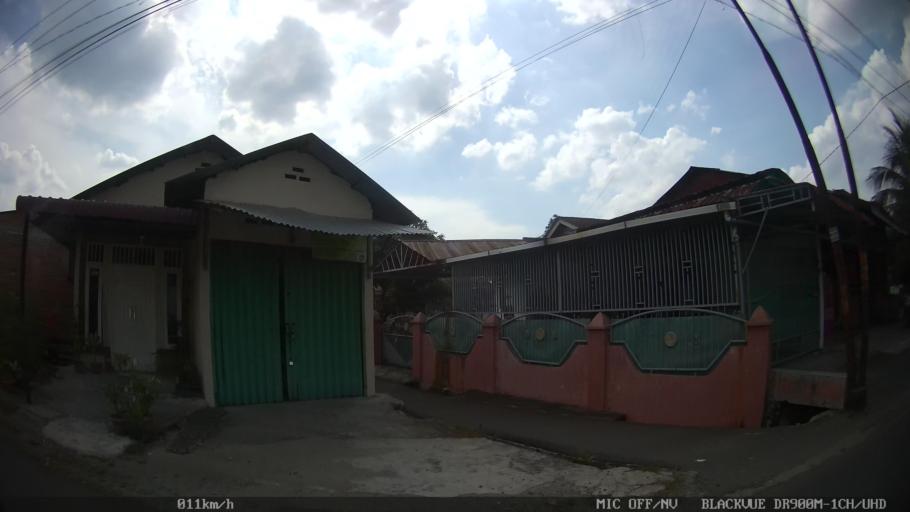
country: ID
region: North Sumatra
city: Binjai
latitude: 3.6154
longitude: 98.4994
